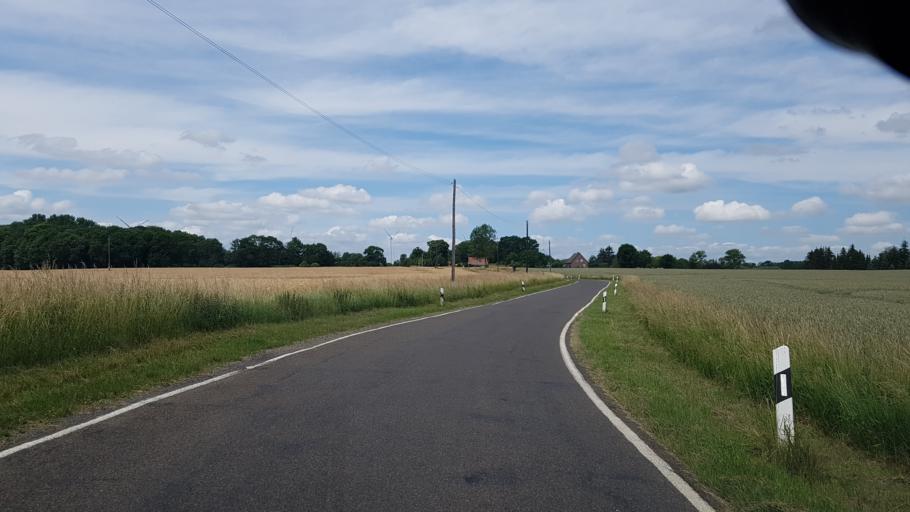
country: DE
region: Mecklenburg-Vorpommern
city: Strasburg
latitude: 53.4429
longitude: 13.7773
